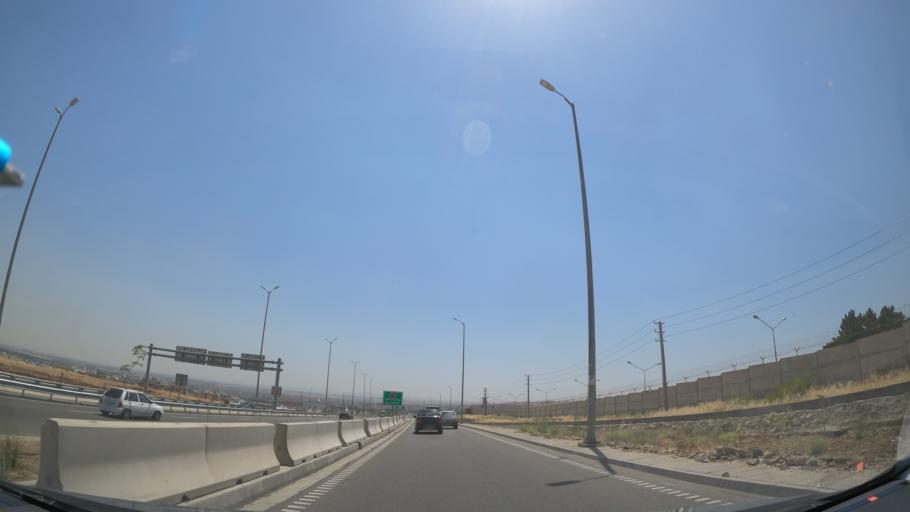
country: IR
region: Tehran
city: Shahr-e Qods
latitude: 35.7480
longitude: 51.1301
